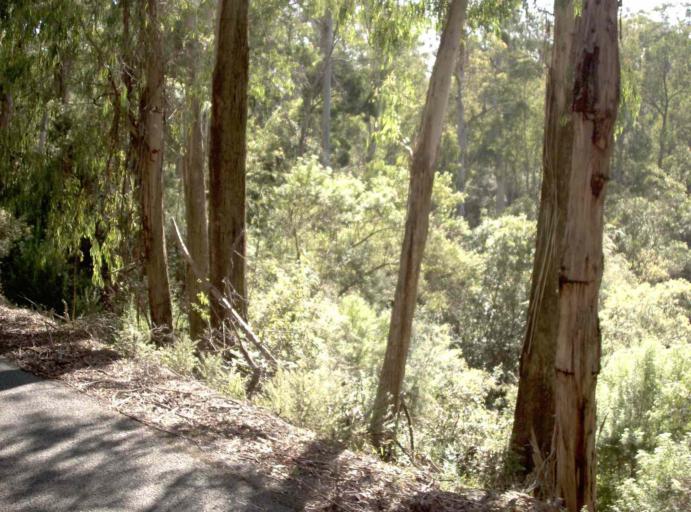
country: AU
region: Victoria
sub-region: East Gippsland
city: Lakes Entrance
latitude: -37.5043
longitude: 148.5417
